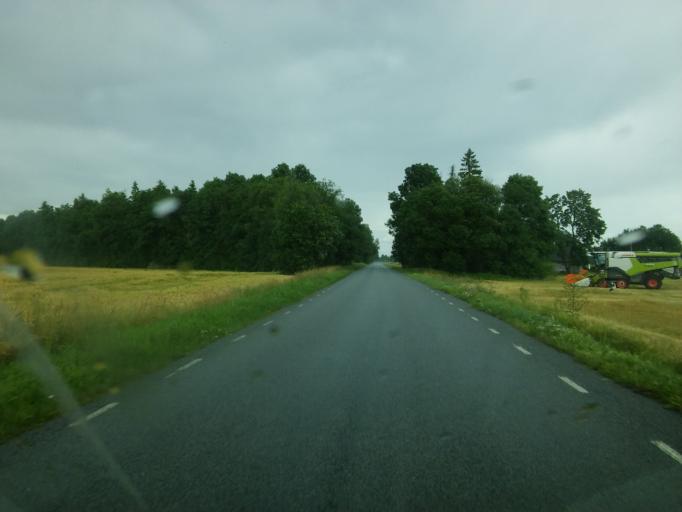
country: EE
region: Raplamaa
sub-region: Maerjamaa vald
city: Marjamaa
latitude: 58.7763
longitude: 24.4768
